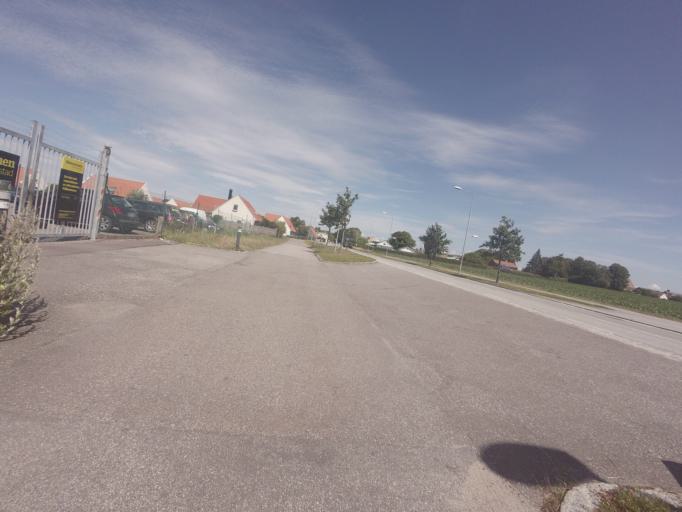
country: SE
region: Skane
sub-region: Malmo
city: Tygelsjo
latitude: 55.5249
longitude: 12.9964
